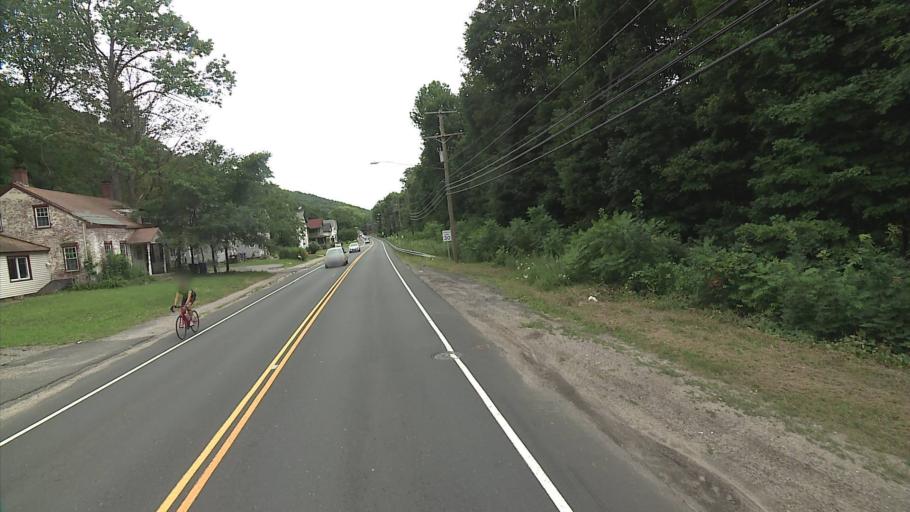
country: US
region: Connecticut
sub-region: Litchfield County
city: Winsted
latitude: 41.9258
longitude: -73.0597
